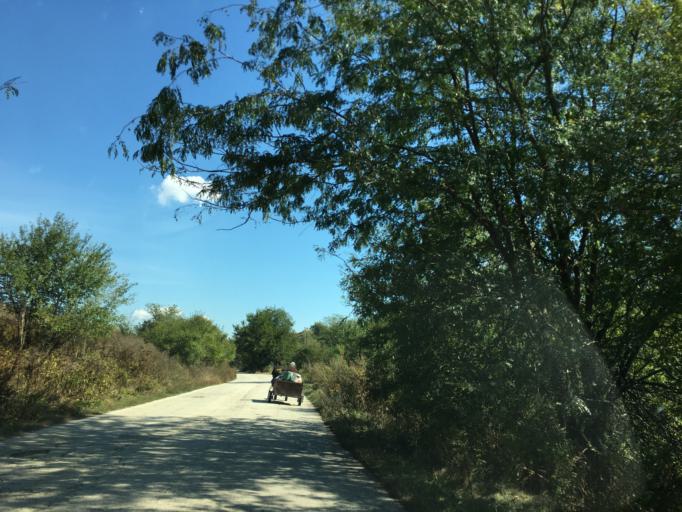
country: BG
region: Pleven
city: Iskur
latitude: 43.5627
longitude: 24.2036
